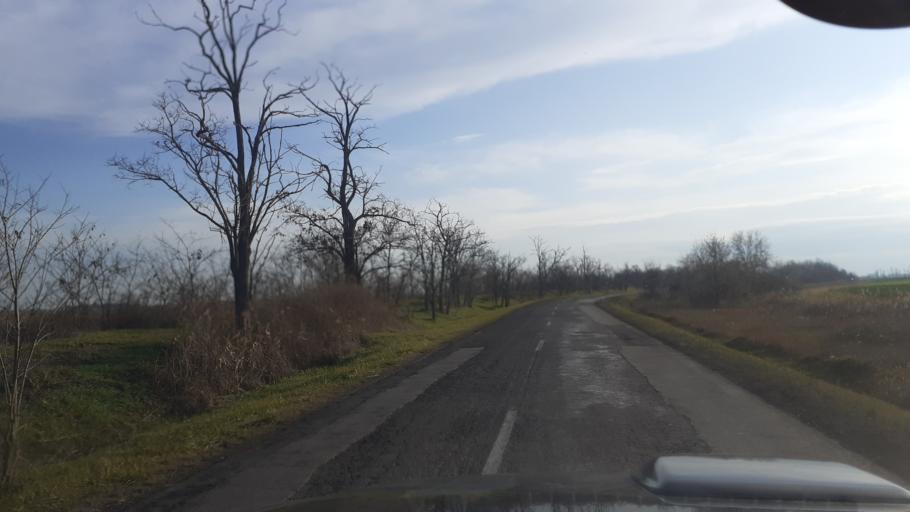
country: HU
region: Pest
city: Domsod
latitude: 47.1079
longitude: 19.0903
